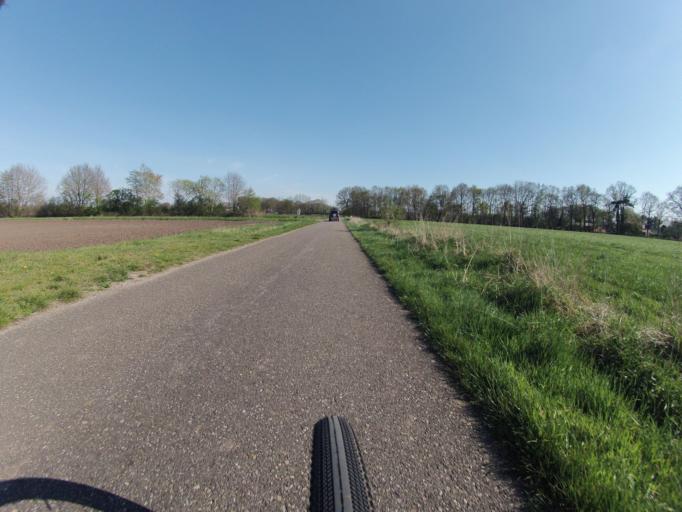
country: DE
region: Lower Saxony
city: Isterberg
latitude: 52.3492
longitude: 7.1654
